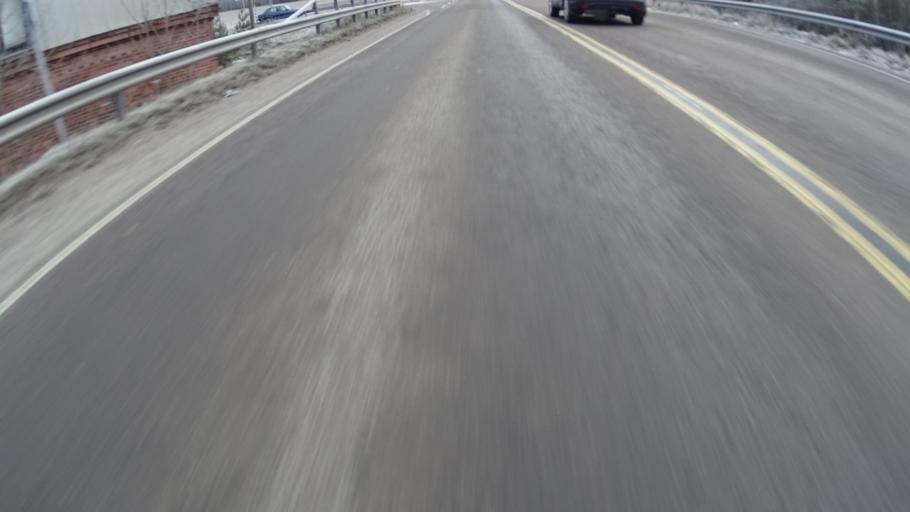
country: FI
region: Uusimaa
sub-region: Helsinki
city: Nurmijaervi
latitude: 60.4305
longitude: 24.7220
